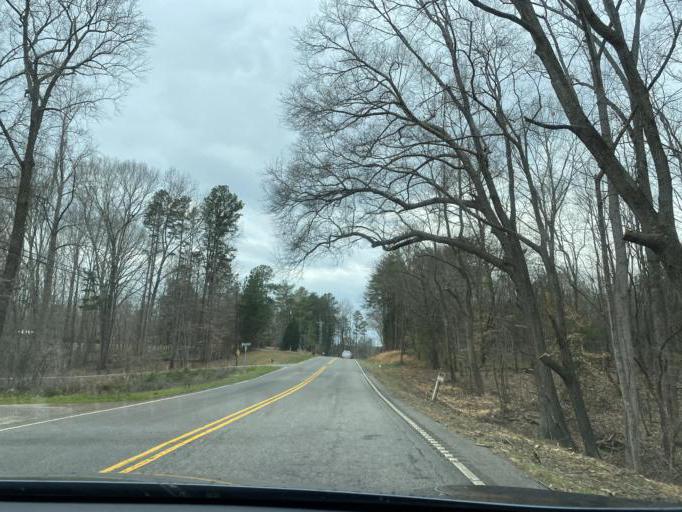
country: US
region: South Carolina
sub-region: Spartanburg County
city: Cowpens
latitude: 35.0165
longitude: -81.7317
